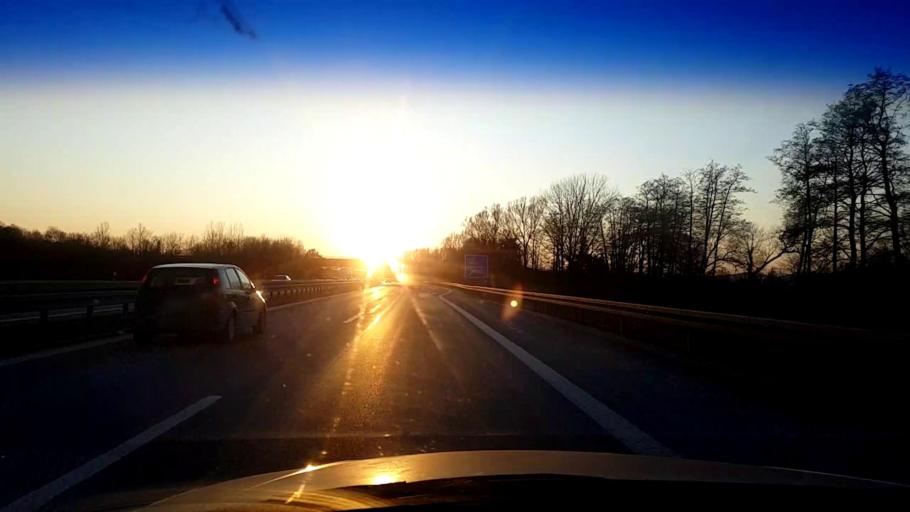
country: DE
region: Bavaria
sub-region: Upper Franconia
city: Gundelsheim
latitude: 49.9303
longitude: 10.9253
